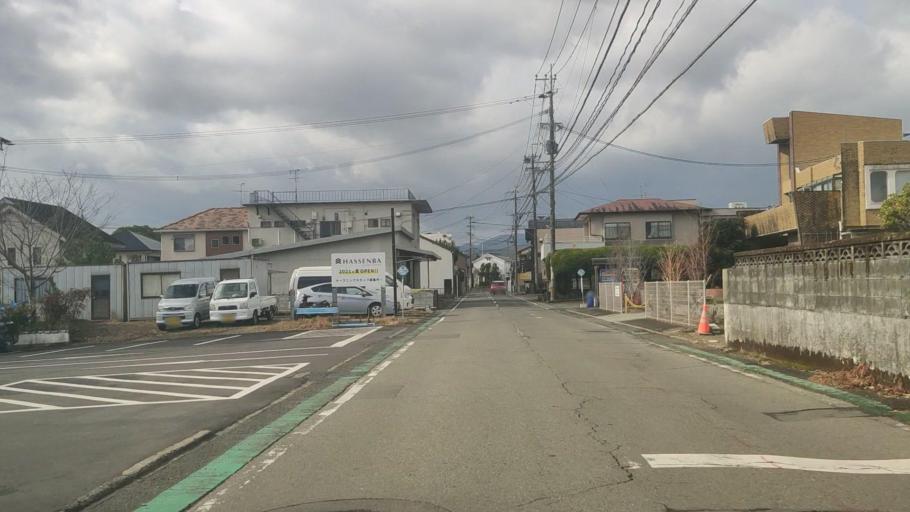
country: JP
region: Kumamoto
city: Hitoyoshi
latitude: 32.2151
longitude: 130.7669
